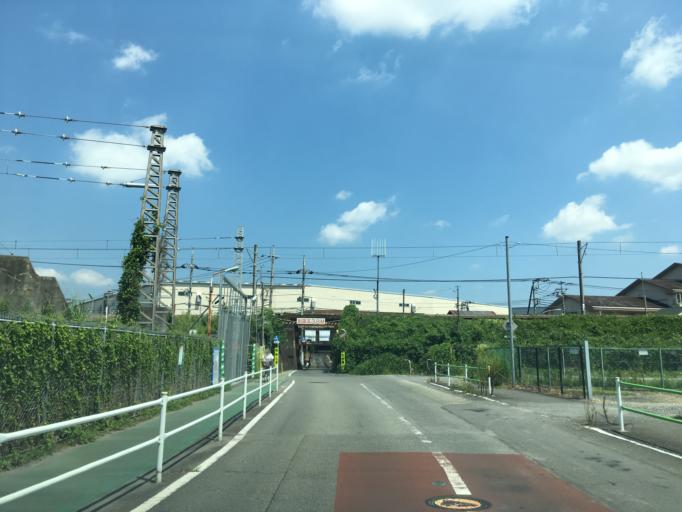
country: JP
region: Tokyo
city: Fussa
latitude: 35.7169
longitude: 139.3504
